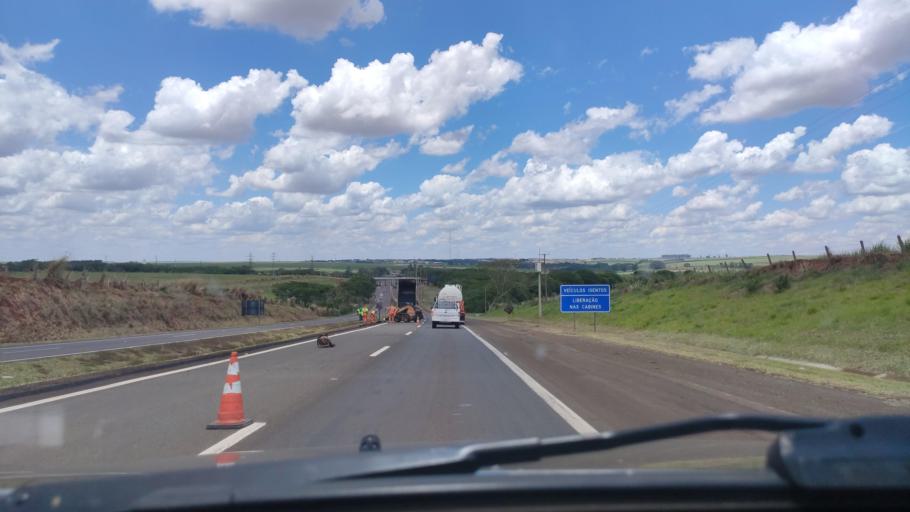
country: BR
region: Sao Paulo
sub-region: Pederneiras
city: Pederneiras
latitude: -22.3145
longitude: -48.7204
